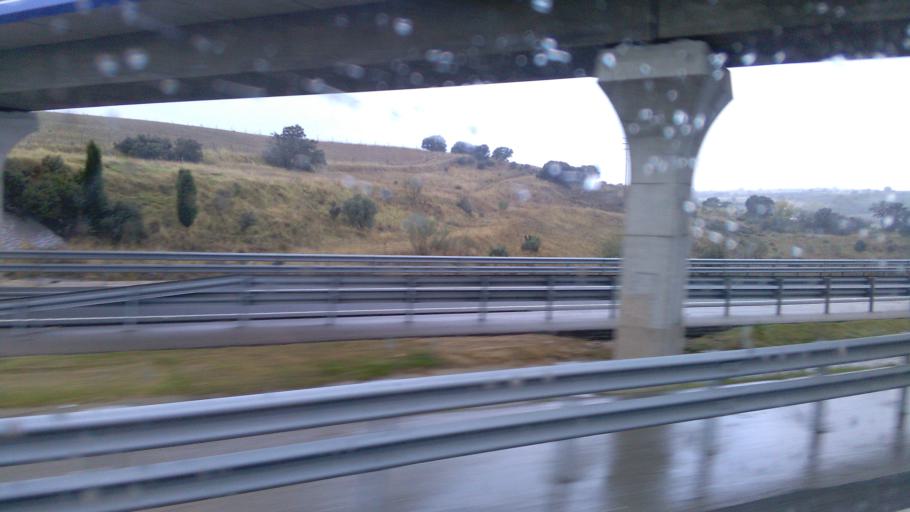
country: ES
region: Madrid
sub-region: Provincia de Madrid
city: Arroyomolinos
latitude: 40.2598
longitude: -3.9452
